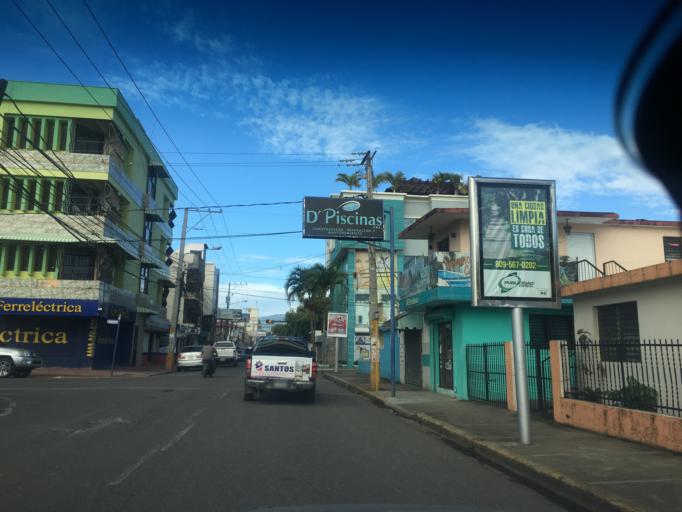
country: DO
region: Duarte
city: San Francisco de Macoris
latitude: 19.2916
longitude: -70.2599
